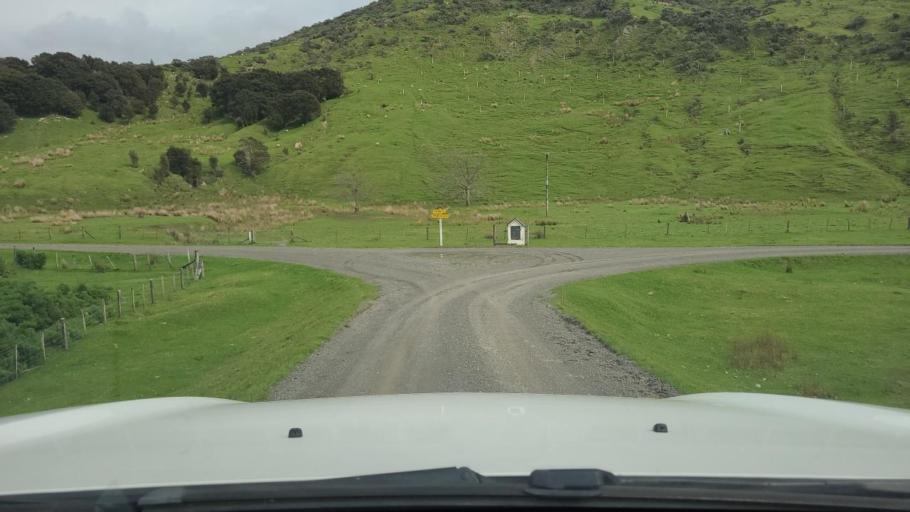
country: NZ
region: Wellington
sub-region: South Wairarapa District
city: Waipawa
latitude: -41.3868
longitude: 175.4510
